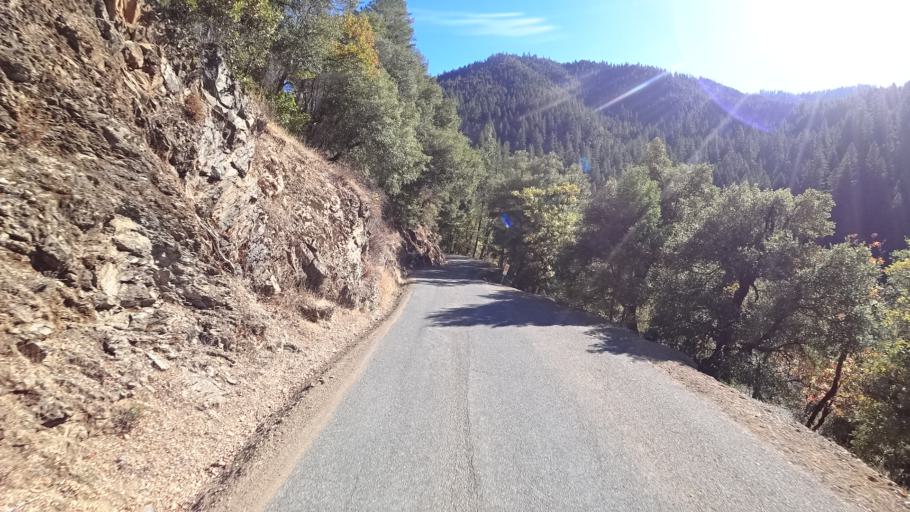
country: US
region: California
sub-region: Siskiyou County
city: Happy Camp
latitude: 41.3038
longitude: -123.1620
